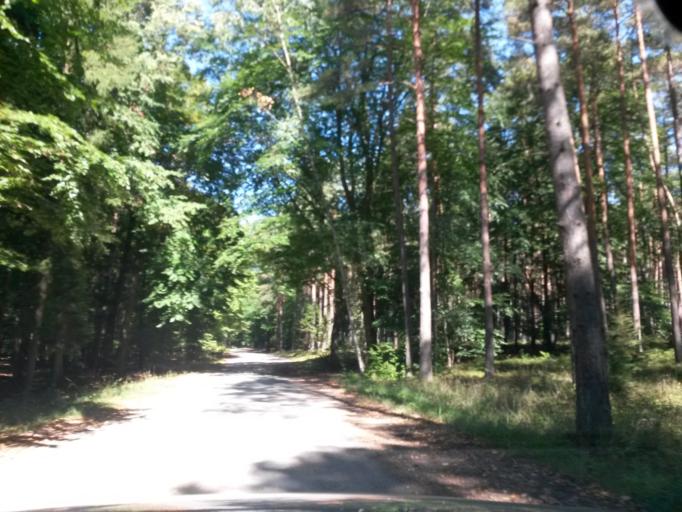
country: DE
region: Brandenburg
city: Templin
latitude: 53.2212
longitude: 13.4556
